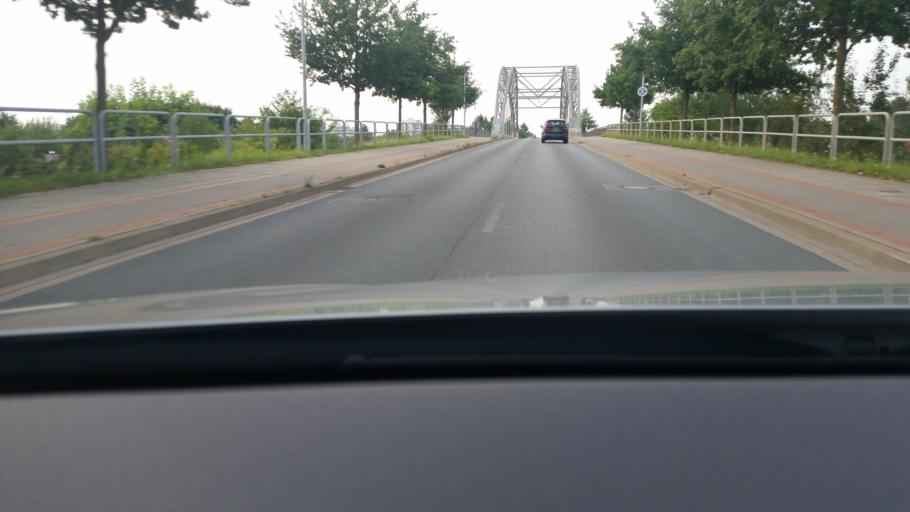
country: DE
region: Lower Saxony
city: Hannover
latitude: 52.4044
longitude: 9.7632
